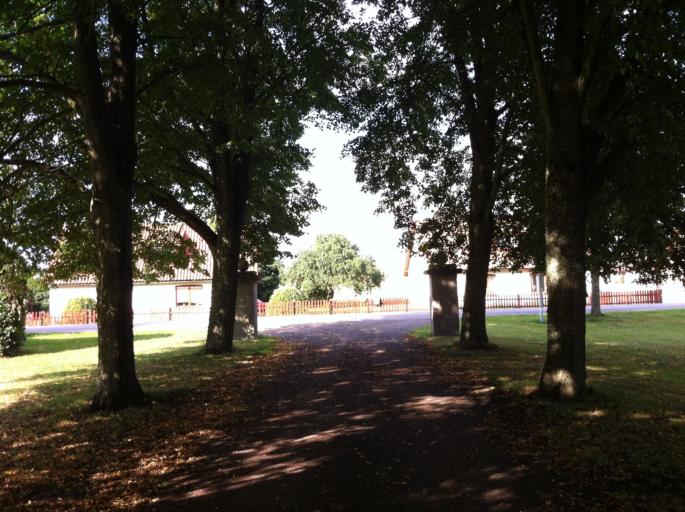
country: SE
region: Skane
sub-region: Landskrona
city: Asmundtorp
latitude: 55.9274
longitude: 12.9973
